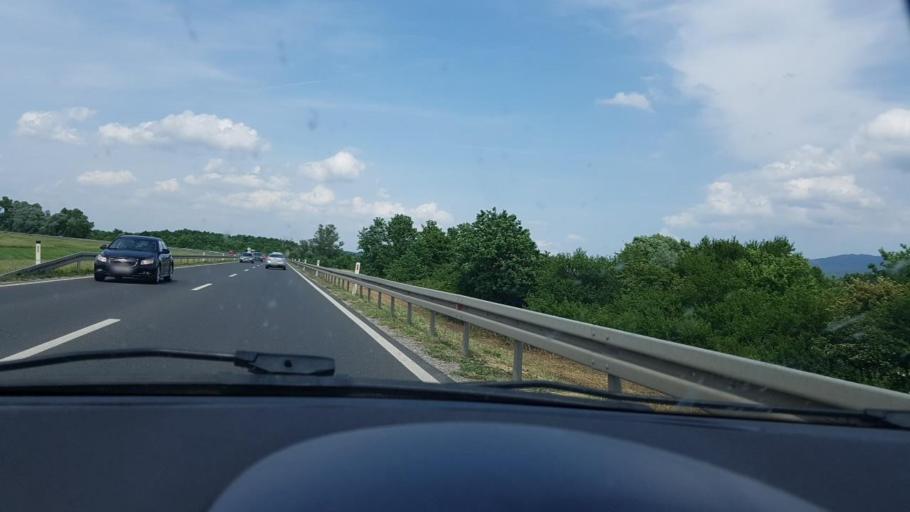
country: HR
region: Zagrebacka
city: Pojatno
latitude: 45.8859
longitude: 15.8219
